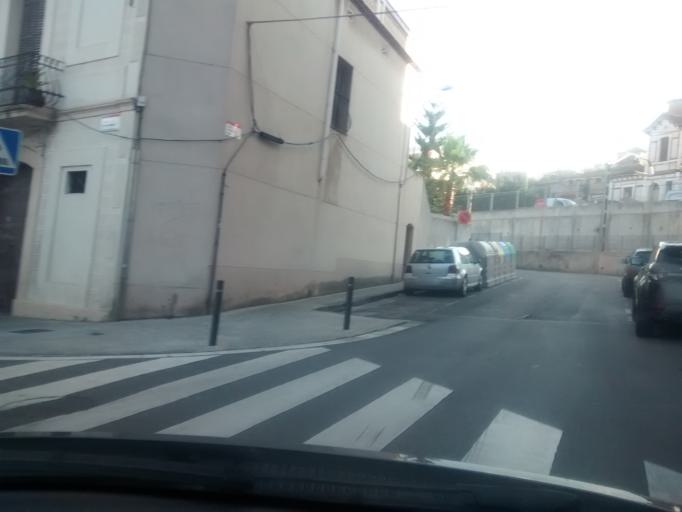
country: ES
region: Catalonia
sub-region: Provincia de Barcelona
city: Sant Vicenc dels Horts
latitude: 41.3934
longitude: 2.0092
